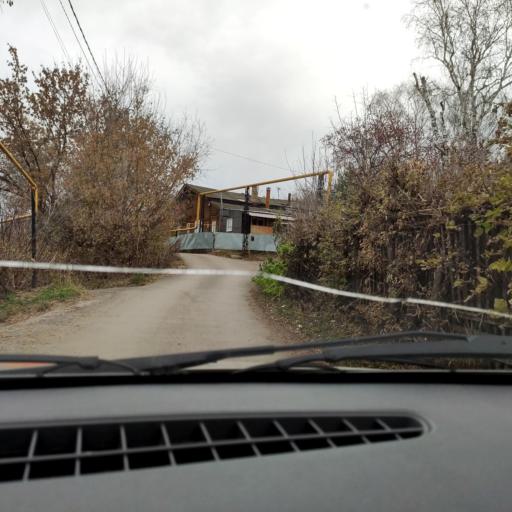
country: RU
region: Bashkortostan
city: Ufa
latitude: 54.7436
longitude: 55.9373
